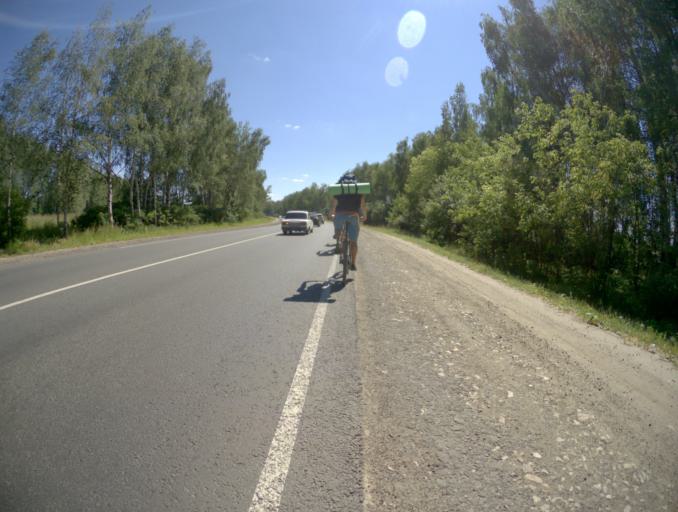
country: RU
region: Nizjnij Novgorod
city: Neklyudovo
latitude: 56.4230
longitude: 43.9935
